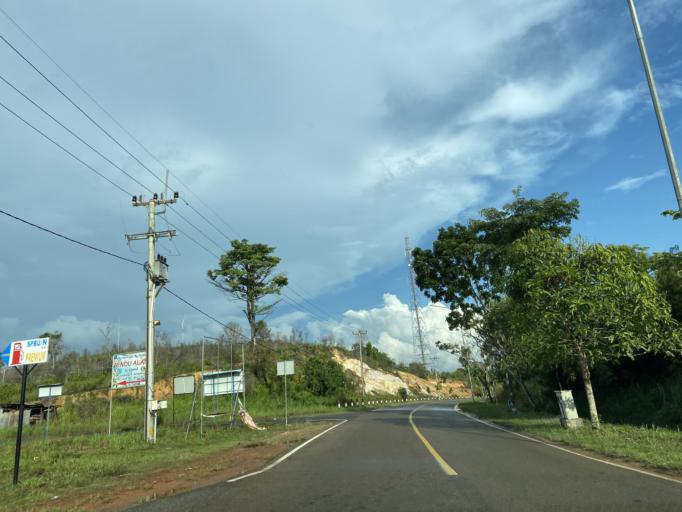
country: ID
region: Riau Islands
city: Tanjungpinang
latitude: 0.9447
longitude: 104.0599
